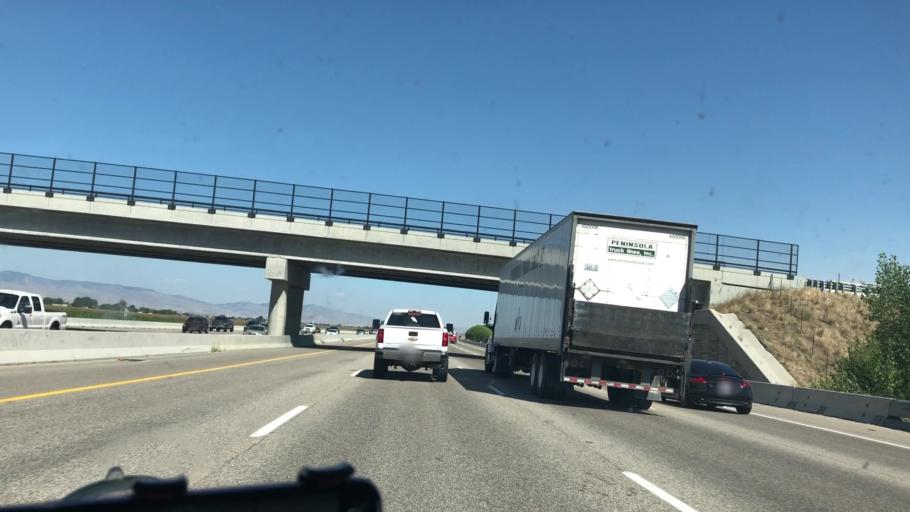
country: US
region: Idaho
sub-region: Canyon County
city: Nampa
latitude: 43.5988
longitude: -116.4931
